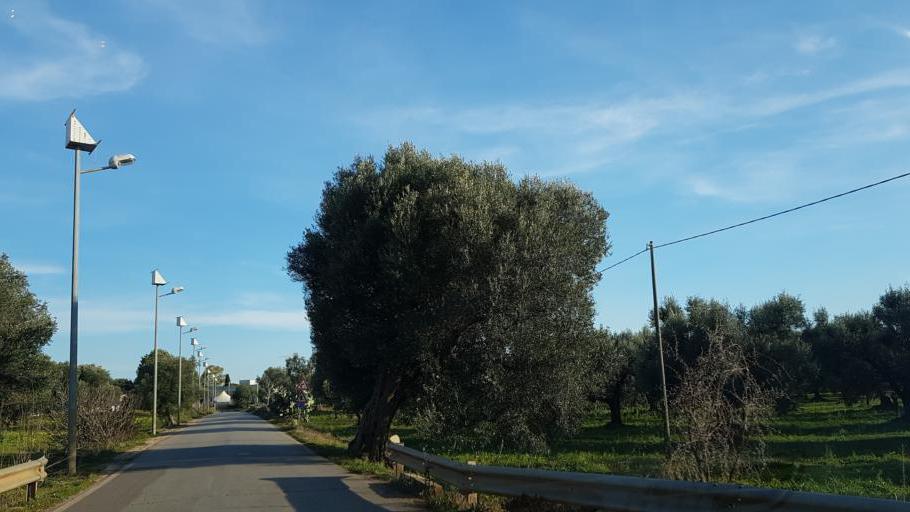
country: IT
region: Apulia
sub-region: Provincia di Brindisi
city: San Vito dei Normanni
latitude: 40.6942
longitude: 17.7600
